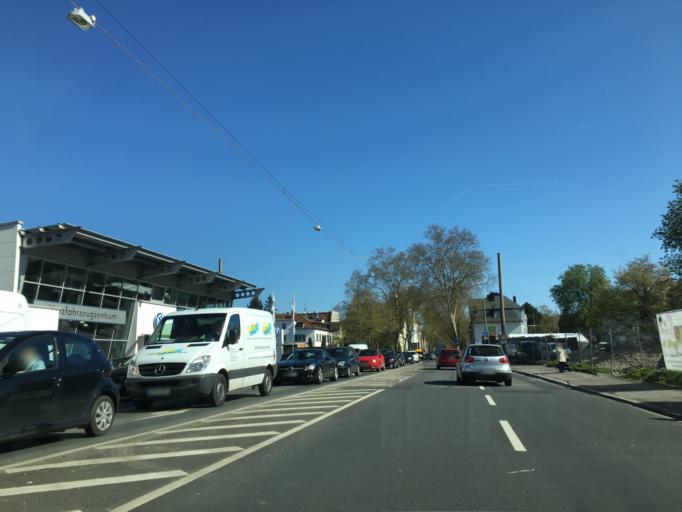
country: DE
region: Hesse
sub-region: Regierungsbezirk Darmstadt
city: Offenbach
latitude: 50.0914
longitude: 8.7510
